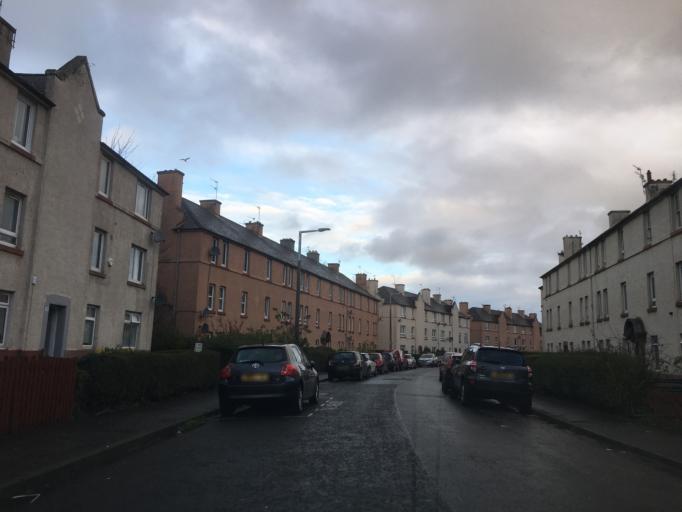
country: GB
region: Scotland
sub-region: Edinburgh
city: Colinton
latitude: 55.9343
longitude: -3.2645
